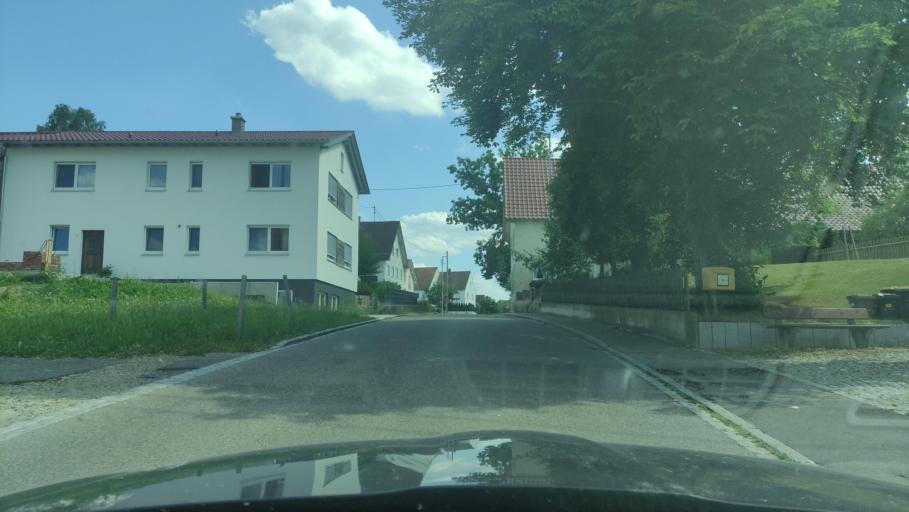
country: DE
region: Bavaria
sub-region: Swabia
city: Deisenhausen
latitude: 48.2891
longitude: 10.3061
